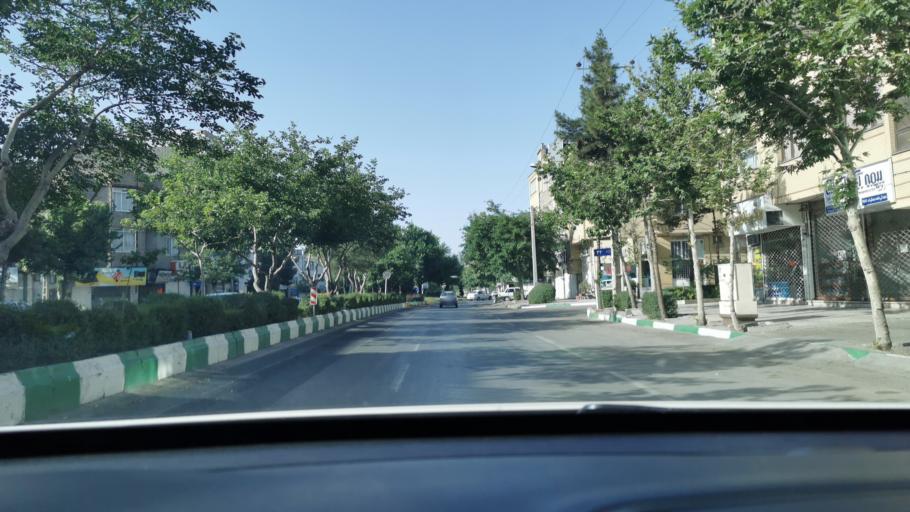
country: IR
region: Razavi Khorasan
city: Mashhad
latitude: 36.3385
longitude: 59.5133
